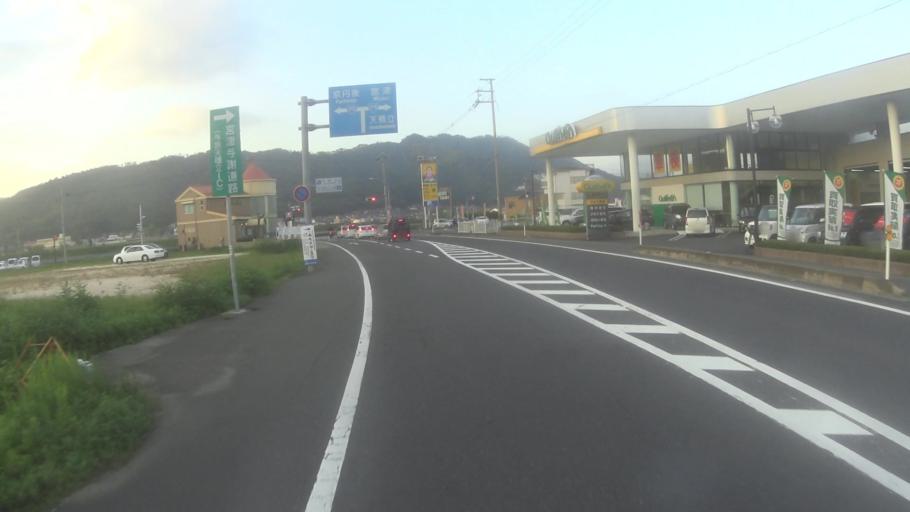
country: JP
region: Kyoto
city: Miyazu
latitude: 35.5338
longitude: 135.1225
